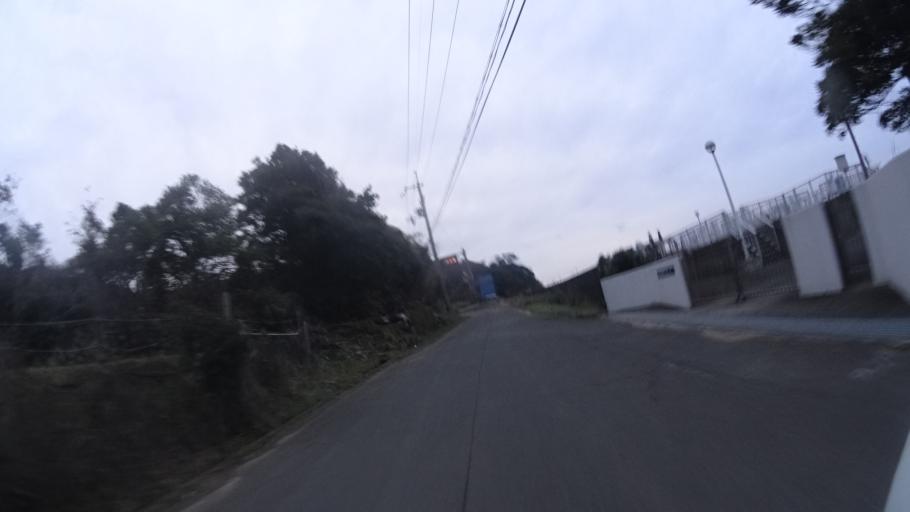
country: JP
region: Kyoto
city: Maizuru
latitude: 35.5661
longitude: 135.4264
